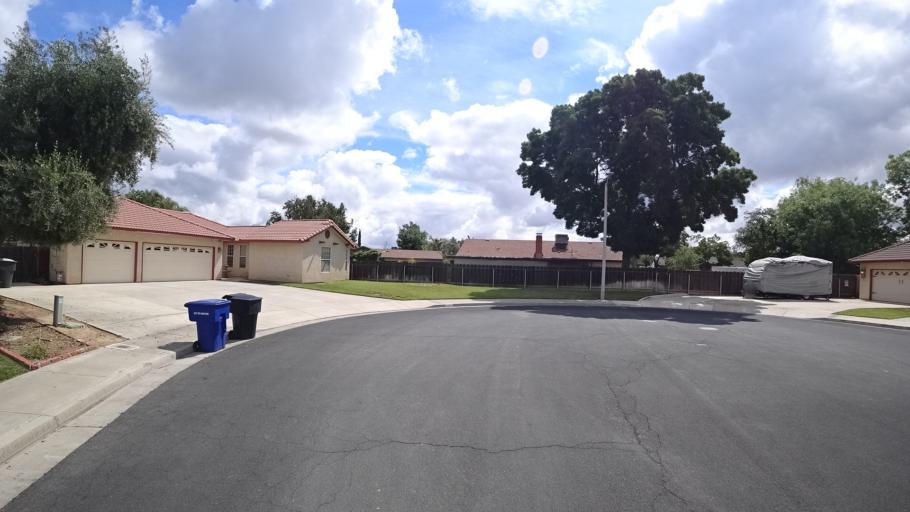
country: US
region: California
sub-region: Kings County
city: Hanford
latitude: 36.3387
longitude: -119.6677
